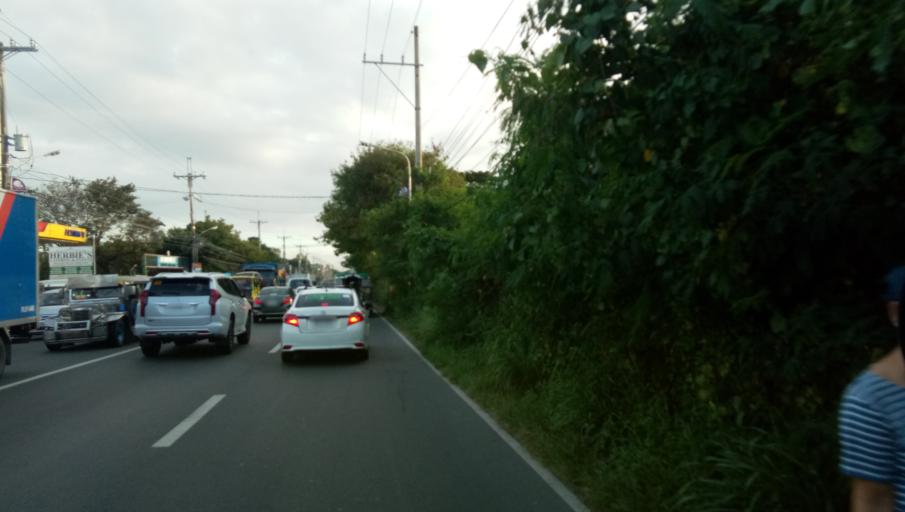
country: PH
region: Calabarzon
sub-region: Province of Cavite
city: Dasmarinas
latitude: 14.3754
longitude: 120.9796
